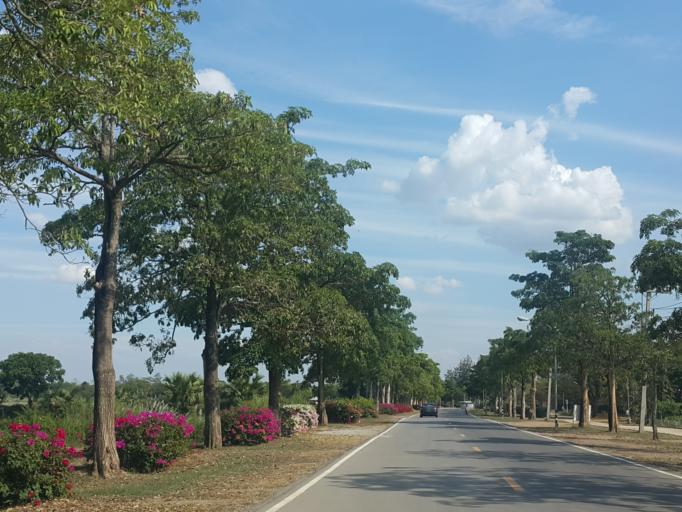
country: TH
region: Sukhothai
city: Si Samrong
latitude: 17.2279
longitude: 99.8281
